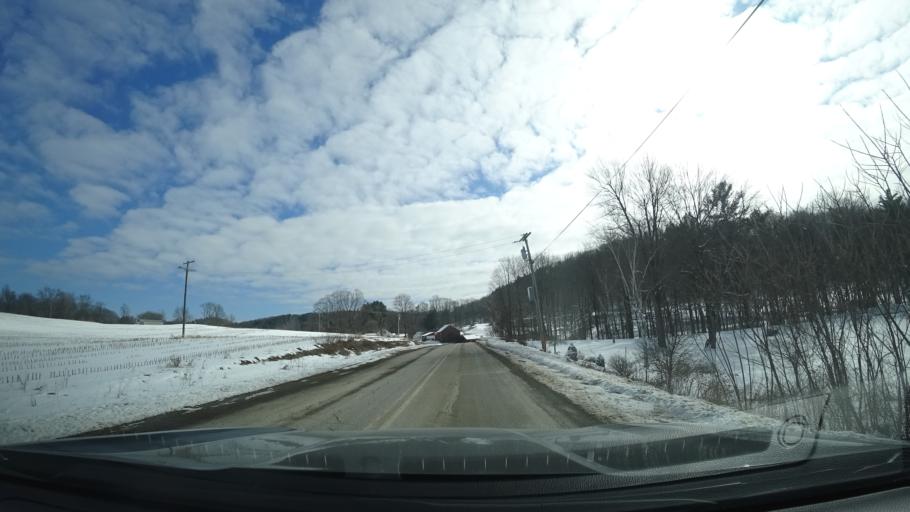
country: US
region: New York
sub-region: Washington County
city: Fort Edward
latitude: 43.2430
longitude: -73.4366
